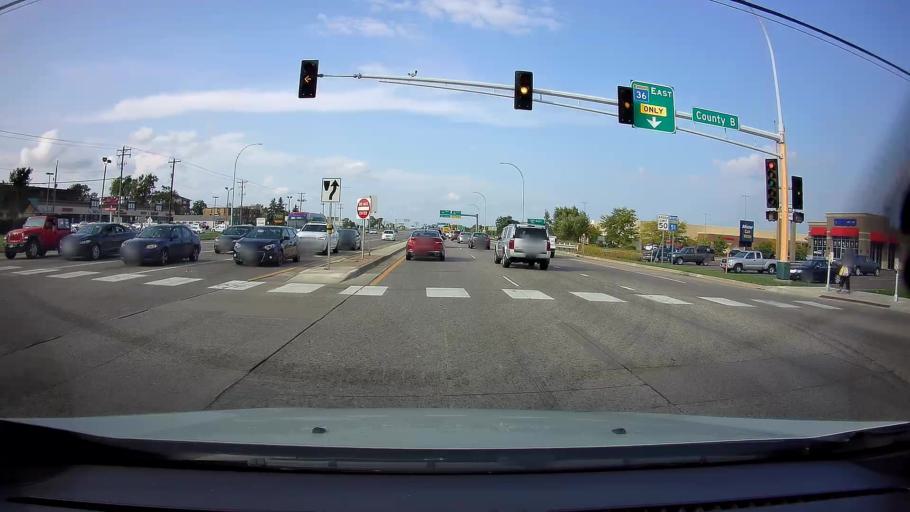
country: US
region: Minnesota
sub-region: Ramsey County
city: Roseville
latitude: 45.0062
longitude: -93.1663
